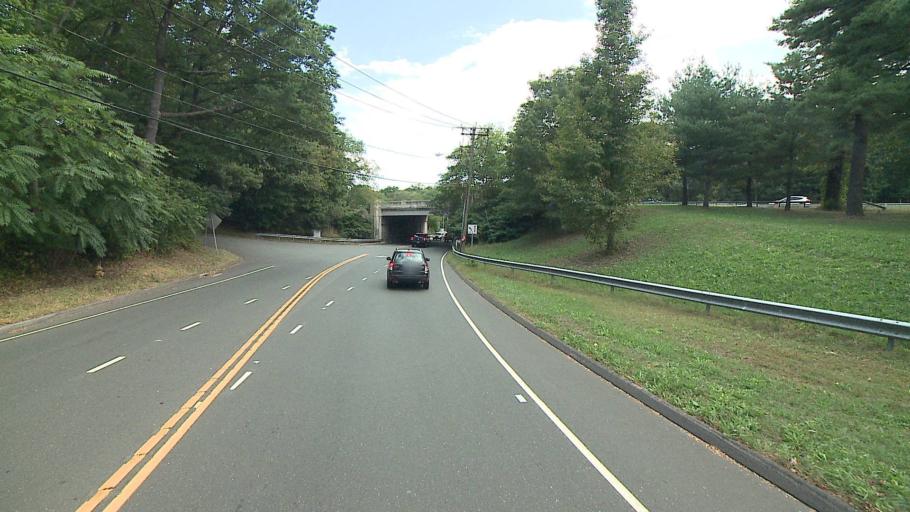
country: US
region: Connecticut
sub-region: Fairfield County
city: Westport
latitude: 41.1645
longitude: -73.3764
